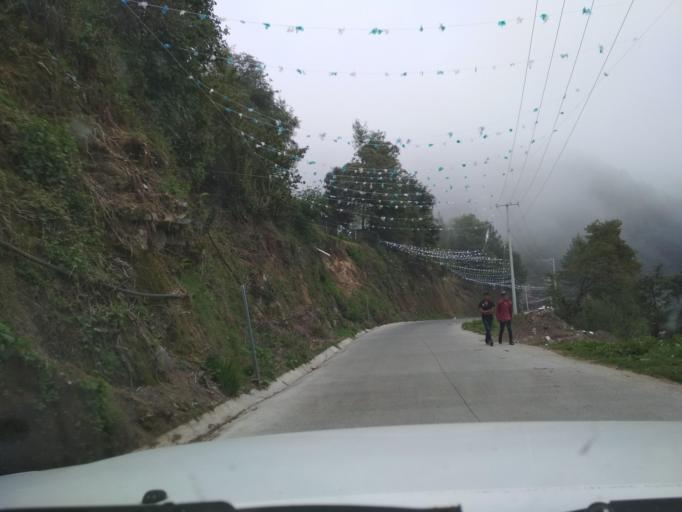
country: MX
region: Veracruz
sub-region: La Perla
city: Chilapa
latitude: 18.9766
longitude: -97.1895
